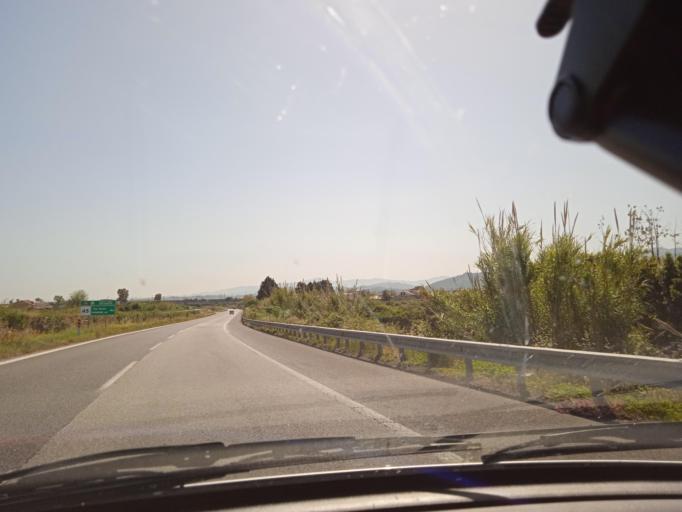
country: IT
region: Sicily
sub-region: Messina
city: Barcellona Pozzo di Gotto
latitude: 38.1636
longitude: 15.2032
